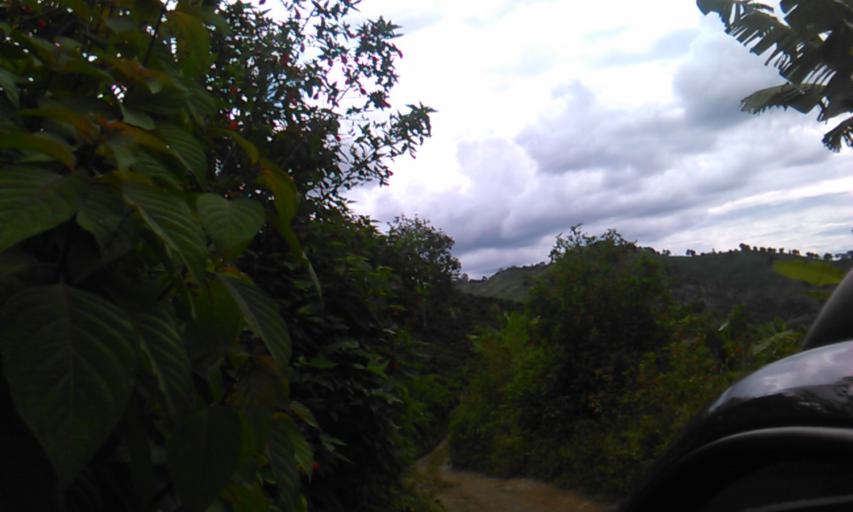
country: CO
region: Quindio
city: Cordoba
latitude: 4.4107
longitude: -75.6833
